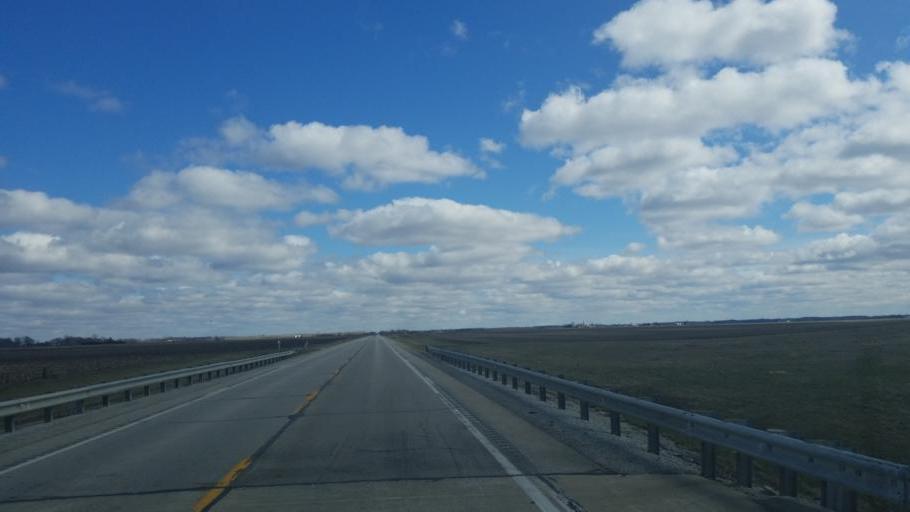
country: US
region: Illinois
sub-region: Douglas County
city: Villa Grove
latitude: 39.7920
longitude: -88.0975
